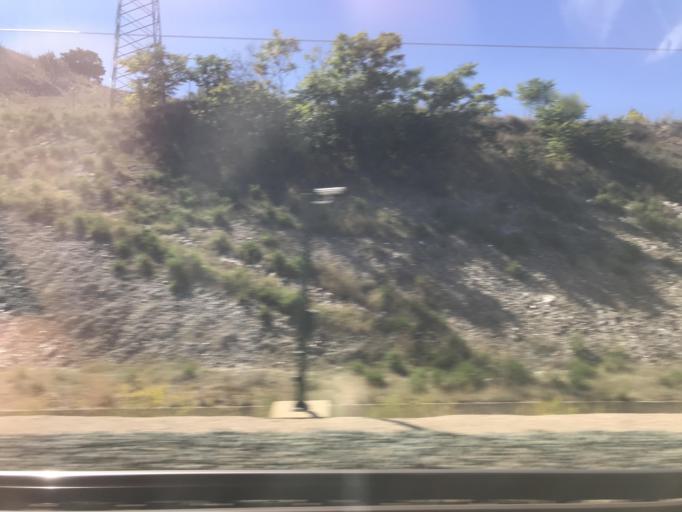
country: ES
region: Castille-La Mancha
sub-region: Provincia de Cuenca
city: Cuenca
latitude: 40.0382
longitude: -2.1491
